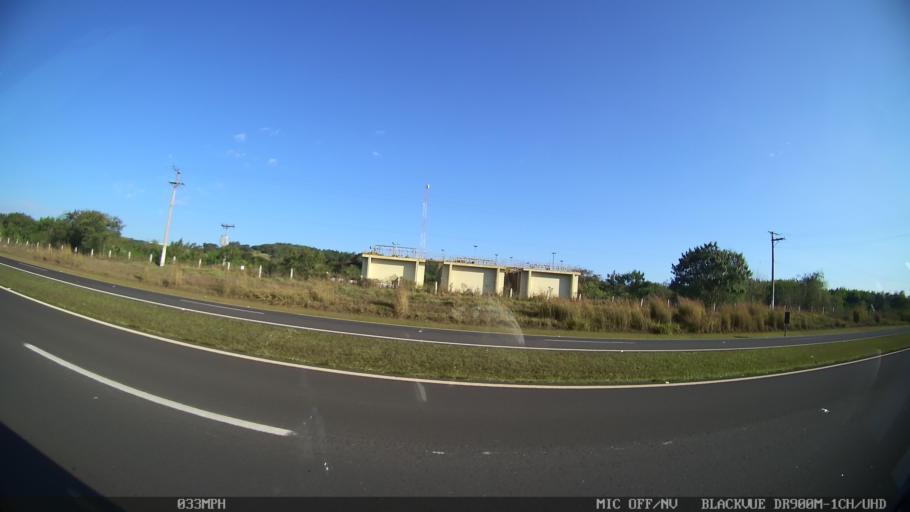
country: BR
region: Sao Paulo
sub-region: Piracicaba
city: Piracicaba
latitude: -22.6994
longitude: -47.6050
